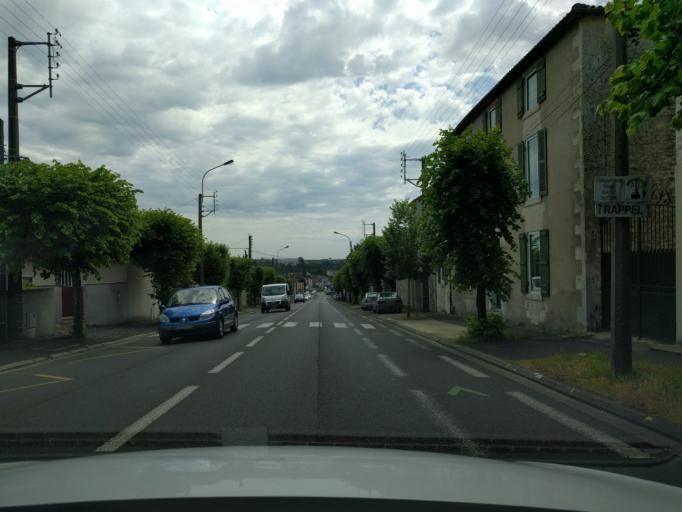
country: FR
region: Poitou-Charentes
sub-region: Departement des Deux-Sevres
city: Niort
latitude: 46.3367
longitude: -0.4771
